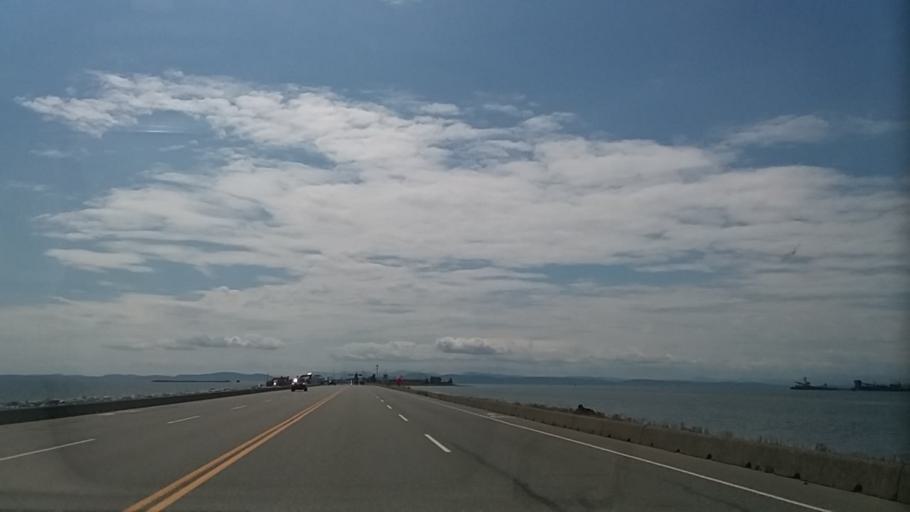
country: US
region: Washington
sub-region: Whatcom County
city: Point Roberts
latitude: 49.0215
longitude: -123.1088
